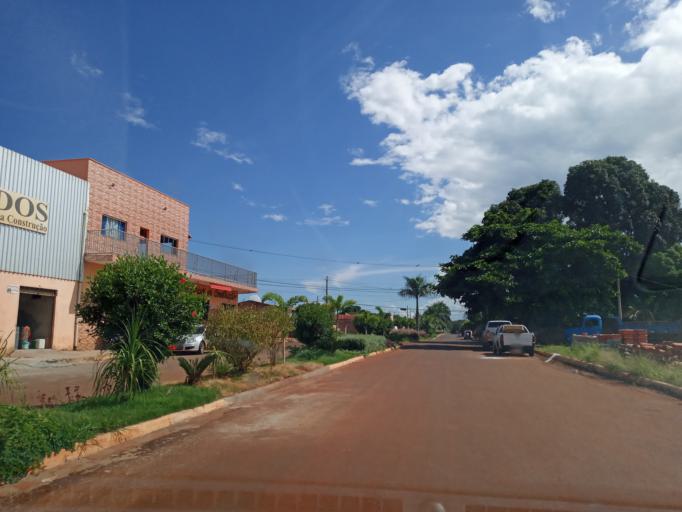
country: BR
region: Goias
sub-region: Itumbiara
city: Itumbiara
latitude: -18.4363
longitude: -49.1829
